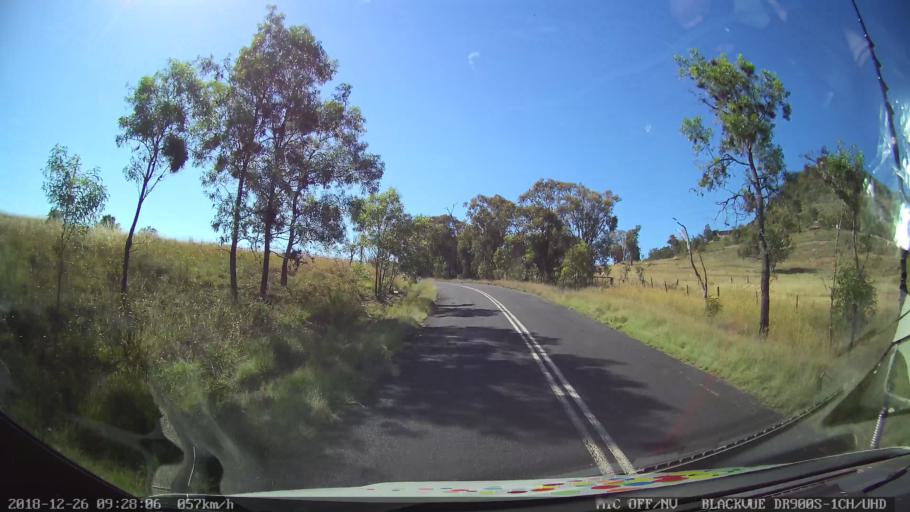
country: AU
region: New South Wales
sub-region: Mid-Western Regional
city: Kandos
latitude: -32.8422
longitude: 150.0202
